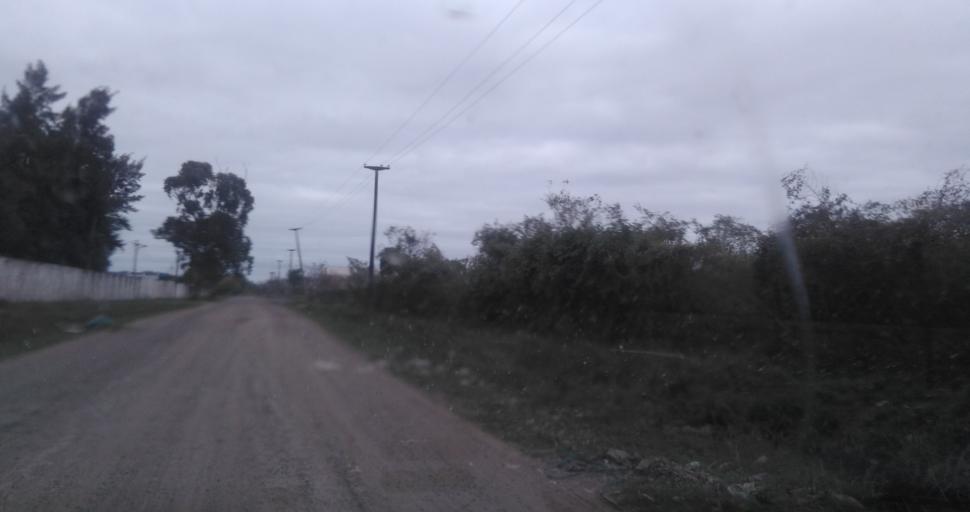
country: AR
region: Chaco
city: Fontana
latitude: -27.4323
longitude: -59.0247
